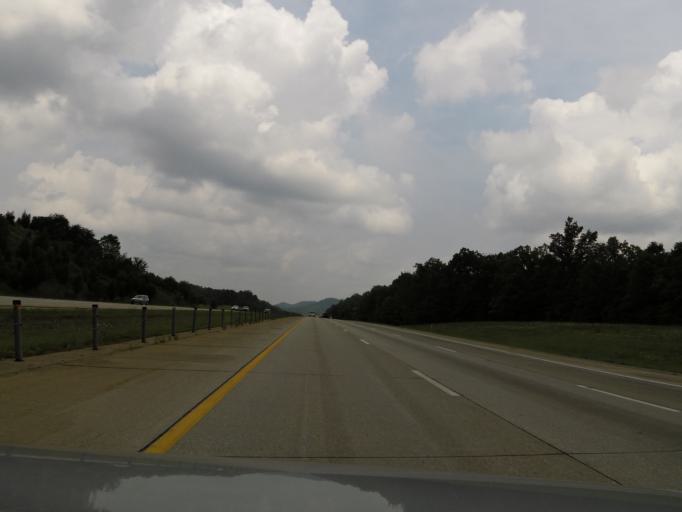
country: US
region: Kentucky
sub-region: Bullitt County
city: Lebanon Junction
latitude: 37.8370
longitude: -85.7168
